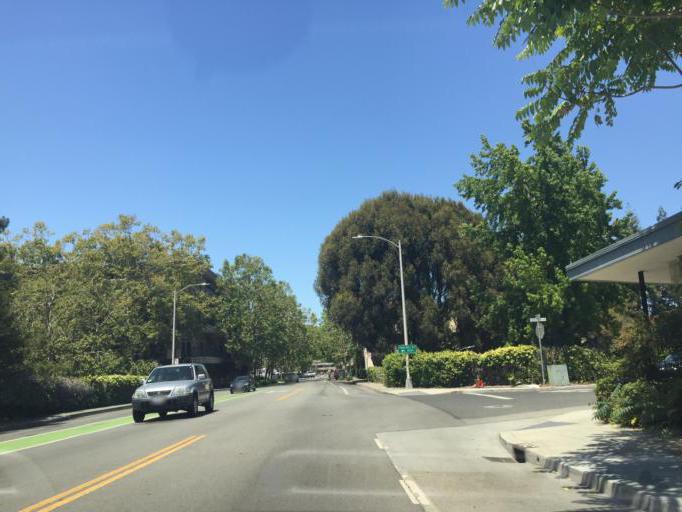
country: US
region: California
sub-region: Santa Clara County
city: Palo Alto
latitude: 37.4266
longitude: -122.1396
